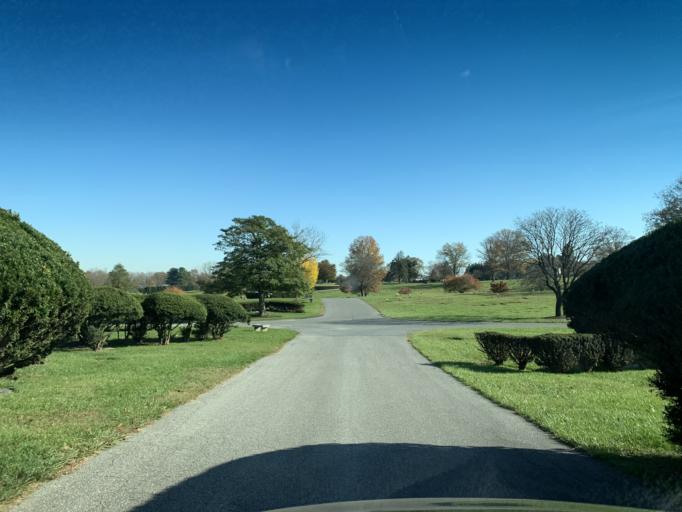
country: US
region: Maryland
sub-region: Baltimore County
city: Timonium
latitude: 39.4583
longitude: -76.6195
